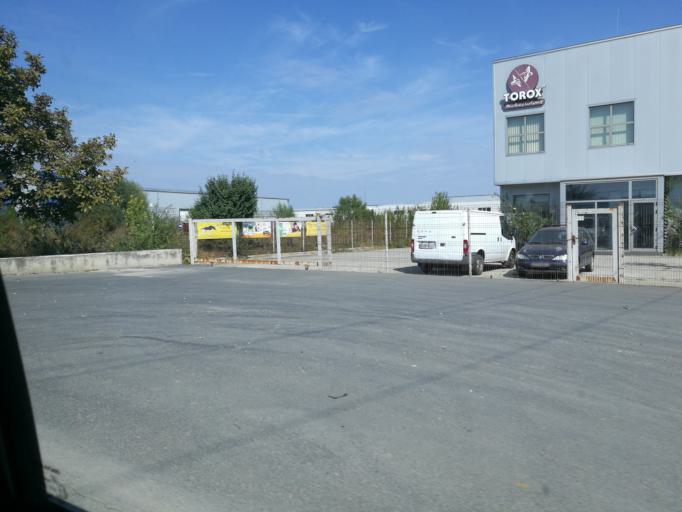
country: RO
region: Ilfov
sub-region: Comuna Otopeni
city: Otopeni
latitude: 44.5424
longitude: 26.0823
